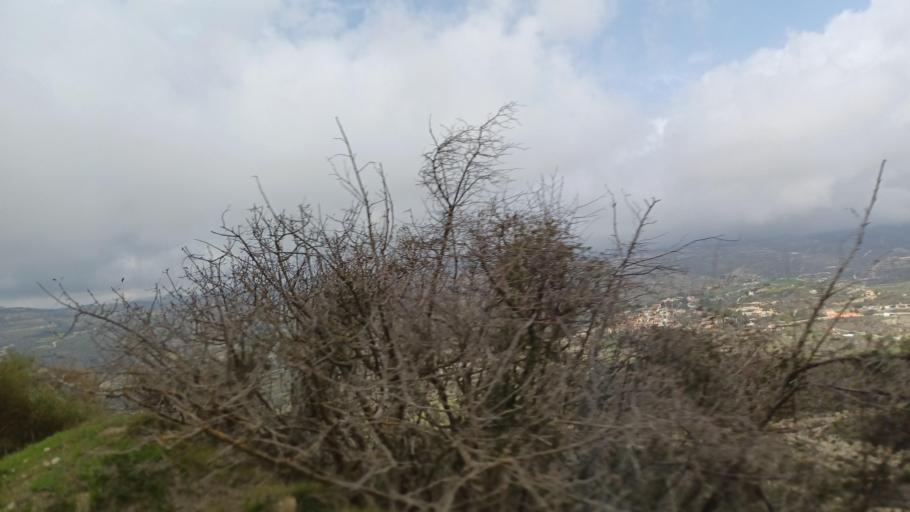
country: CY
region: Limassol
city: Pachna
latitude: 34.7687
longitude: 32.8284
